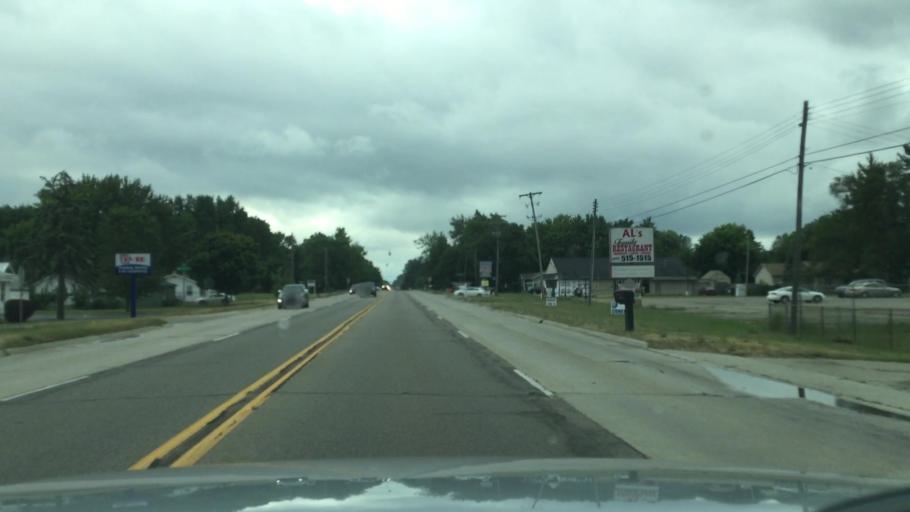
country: US
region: Michigan
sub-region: Genesee County
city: Burton
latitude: 43.0607
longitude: -83.6164
